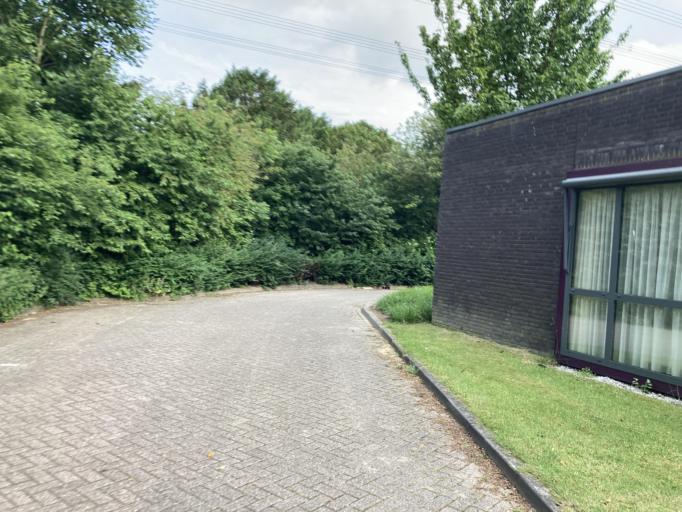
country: NL
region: North Brabant
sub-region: Gemeente Eindhoven
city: Eindhoven
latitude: 51.4719
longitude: 5.4556
